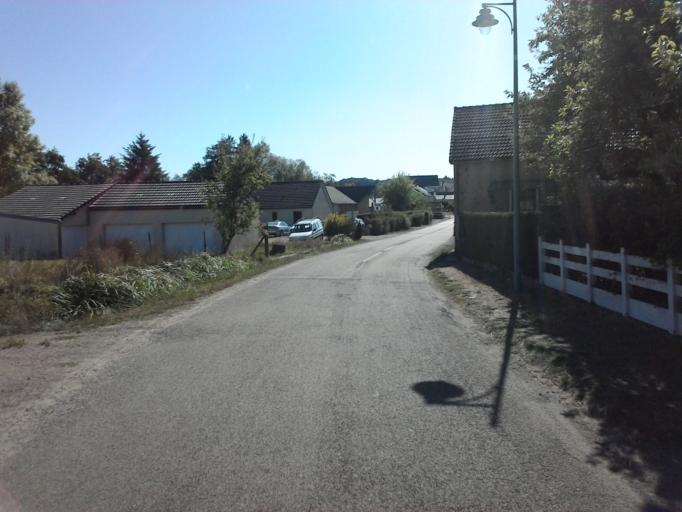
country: FR
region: Bourgogne
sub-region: Departement de la Nievre
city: Lormes
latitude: 47.2640
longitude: 3.9384
